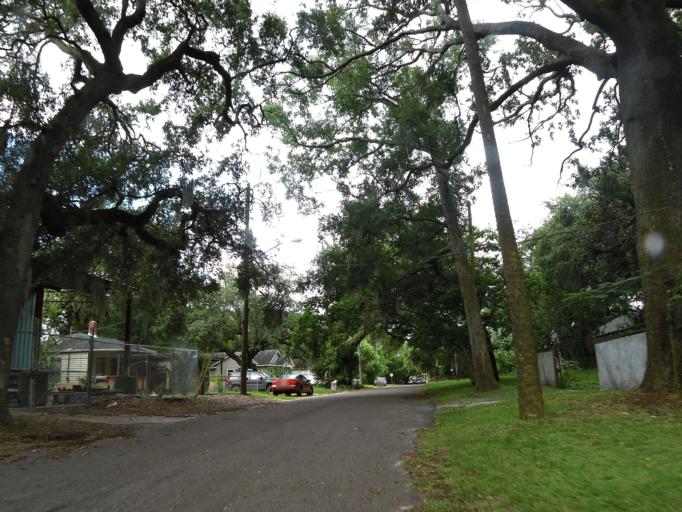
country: US
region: Florida
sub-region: Duval County
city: Jacksonville
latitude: 30.3508
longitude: -81.6293
